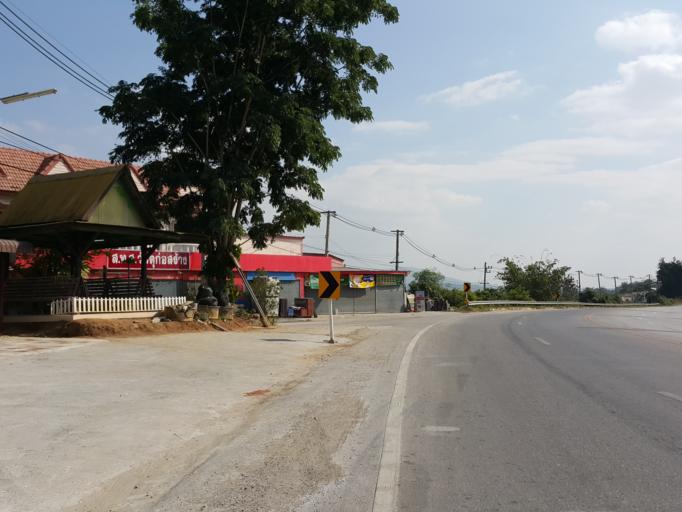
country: TH
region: Lamphun
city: Ban Hong
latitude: 18.2876
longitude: 98.8169
